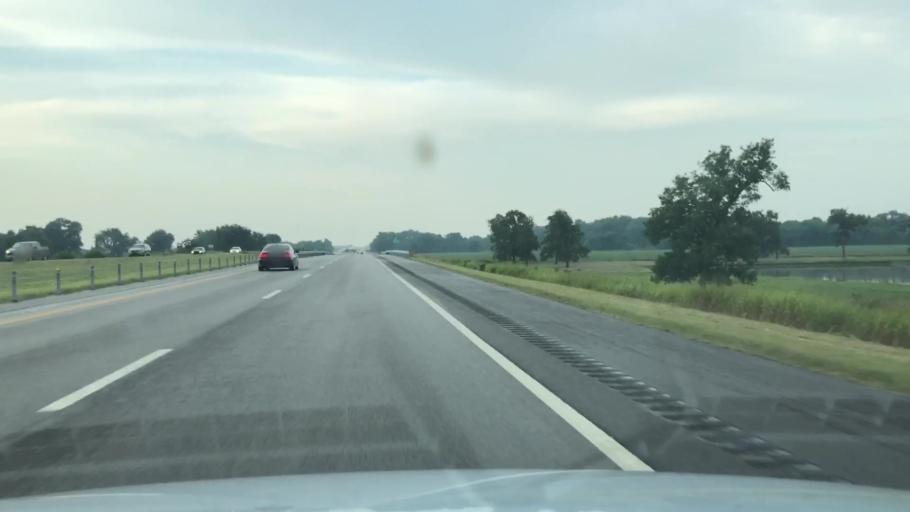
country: US
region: Oklahoma
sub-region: Washington County
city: Bartlesville
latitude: 36.6515
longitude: -95.9356
